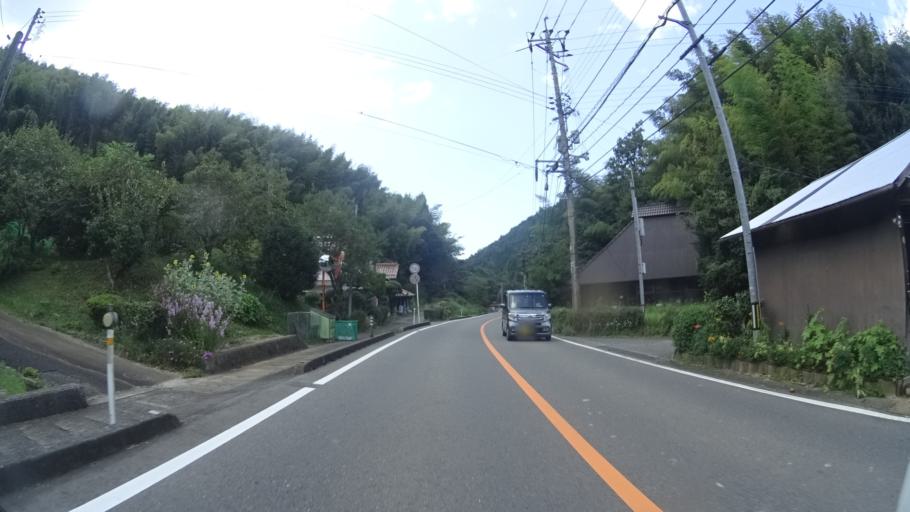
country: JP
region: Yamaguchi
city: Hagi
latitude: 34.4368
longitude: 131.4636
